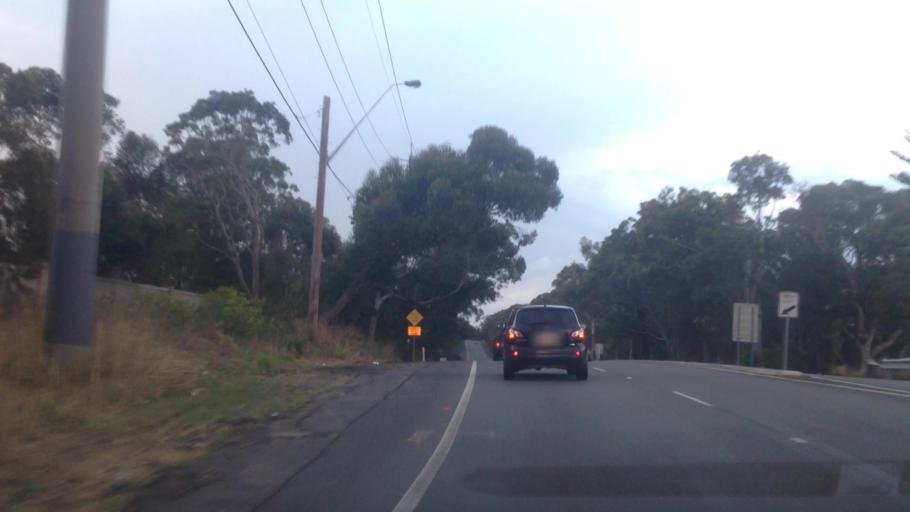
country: AU
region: New South Wales
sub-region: Wyong Shire
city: Kanwal
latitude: -33.2509
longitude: 151.4909
